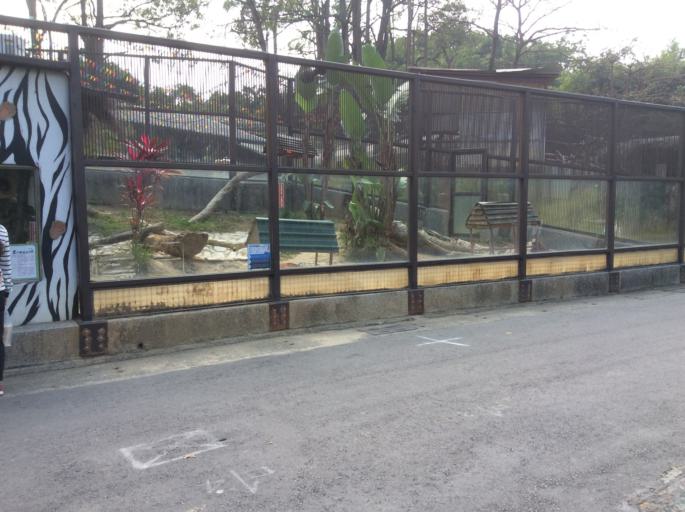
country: TW
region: Kaohsiung
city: Kaohsiung
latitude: 22.6350
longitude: 120.2758
